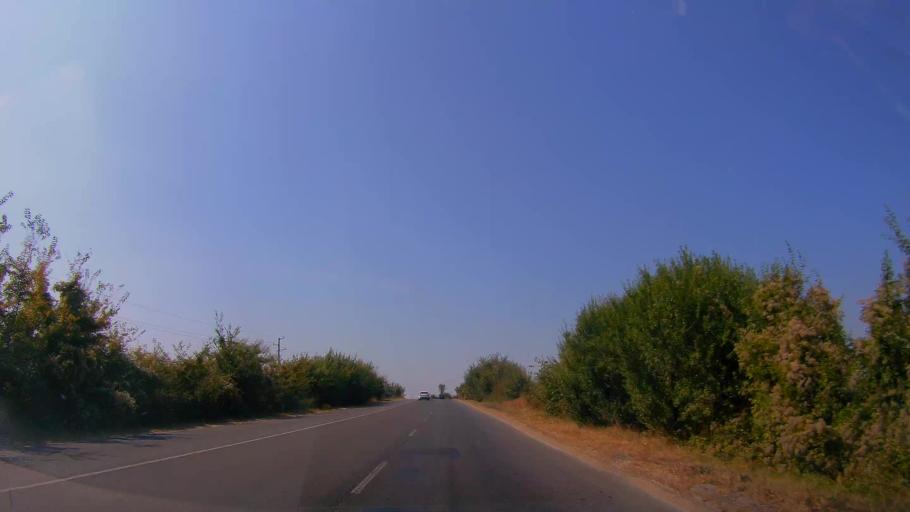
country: BG
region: Ruse
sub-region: Obshtina Vetovo
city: Senovo
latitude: 43.5618
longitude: 26.3629
